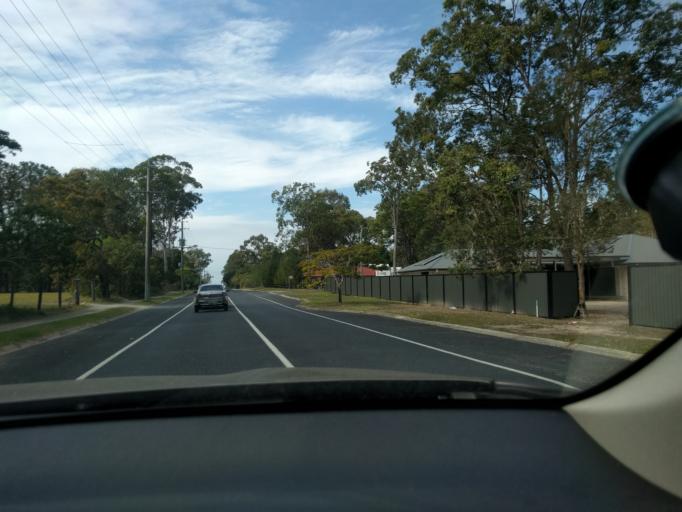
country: AU
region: Queensland
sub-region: Moreton Bay
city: Burpengary
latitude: -27.1407
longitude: 152.9929
